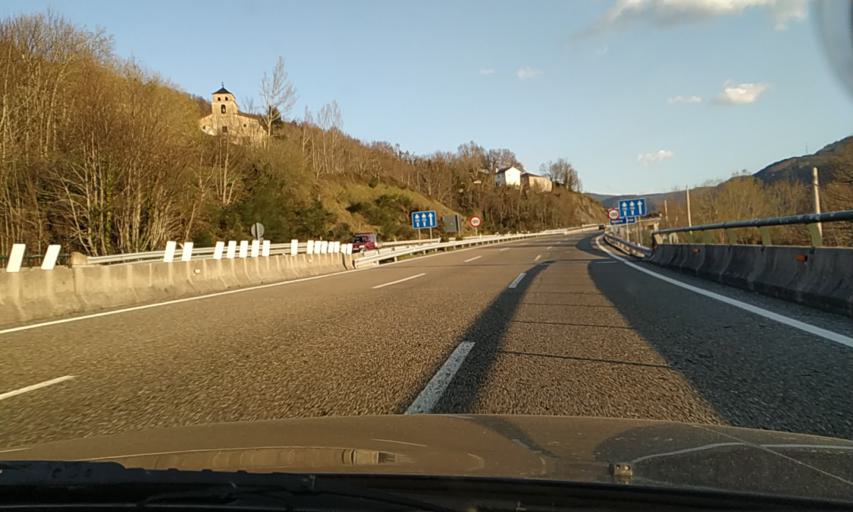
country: ES
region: Galicia
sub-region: Provincia de Lugo
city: San Roman
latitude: 42.7611
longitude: -7.0775
